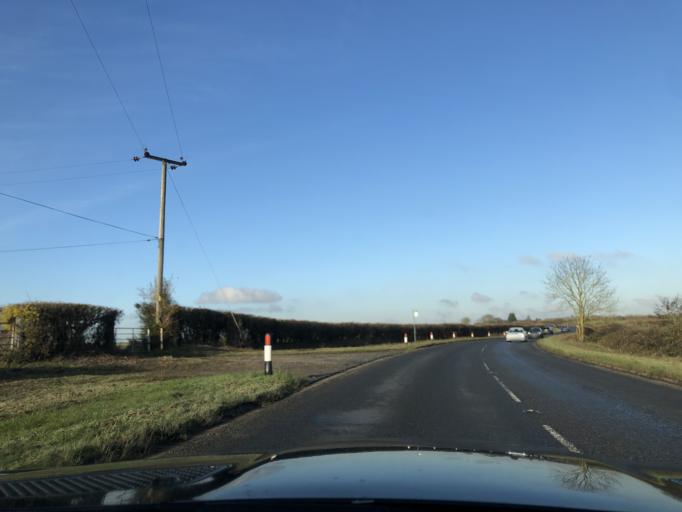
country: GB
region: England
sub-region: Buckinghamshire
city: Marlow
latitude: 51.6002
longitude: -0.7699
